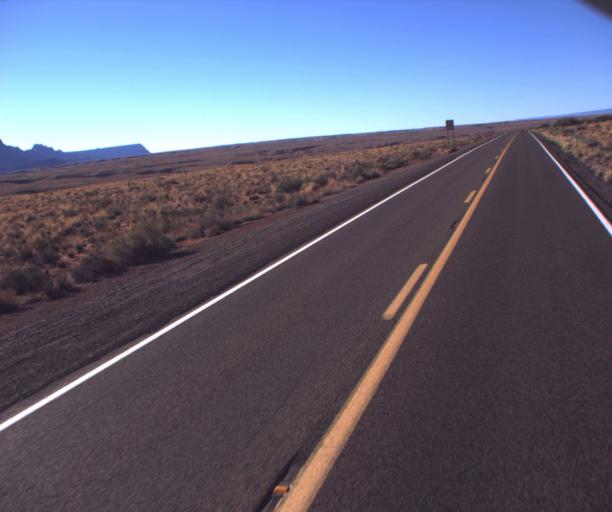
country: US
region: Arizona
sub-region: Coconino County
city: Page
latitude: 36.7950
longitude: -111.6807
